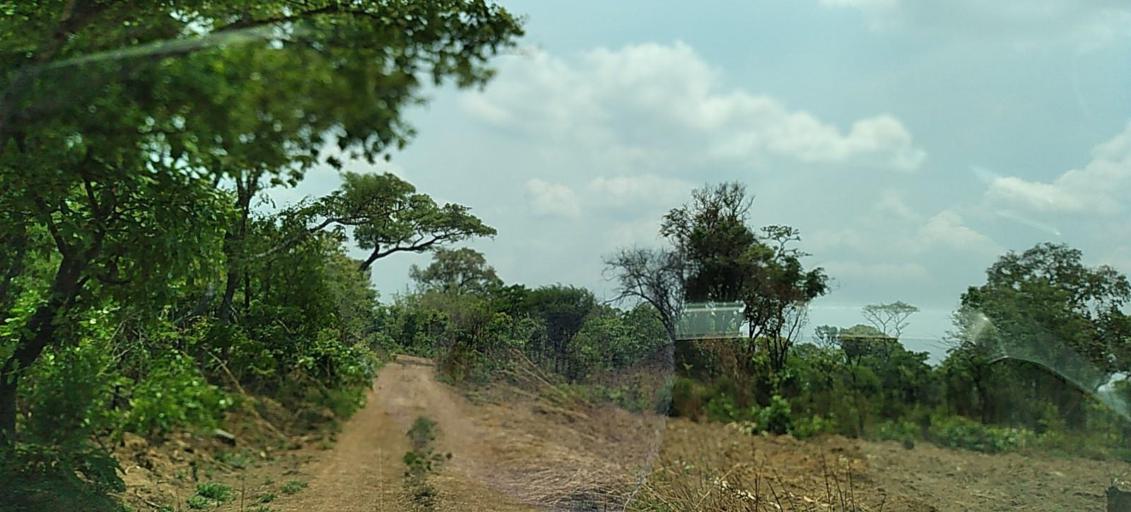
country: ZM
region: Copperbelt
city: Chililabombwe
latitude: -12.3794
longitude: 27.6441
